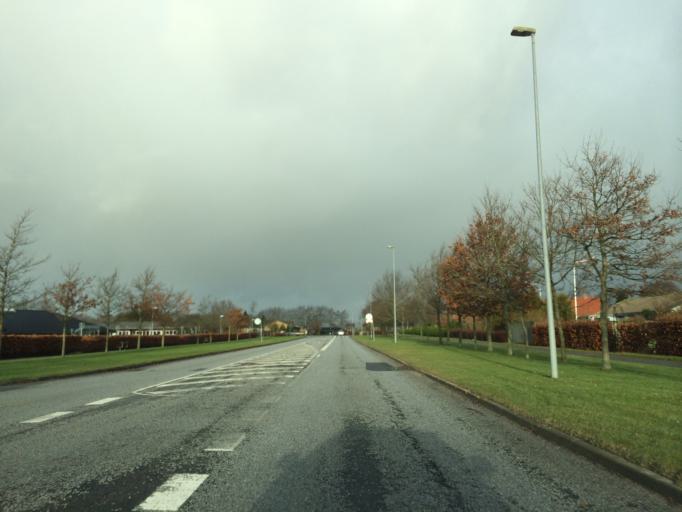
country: DK
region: Central Jutland
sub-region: Herning Kommune
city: Vildbjerg
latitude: 56.1918
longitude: 8.7618
